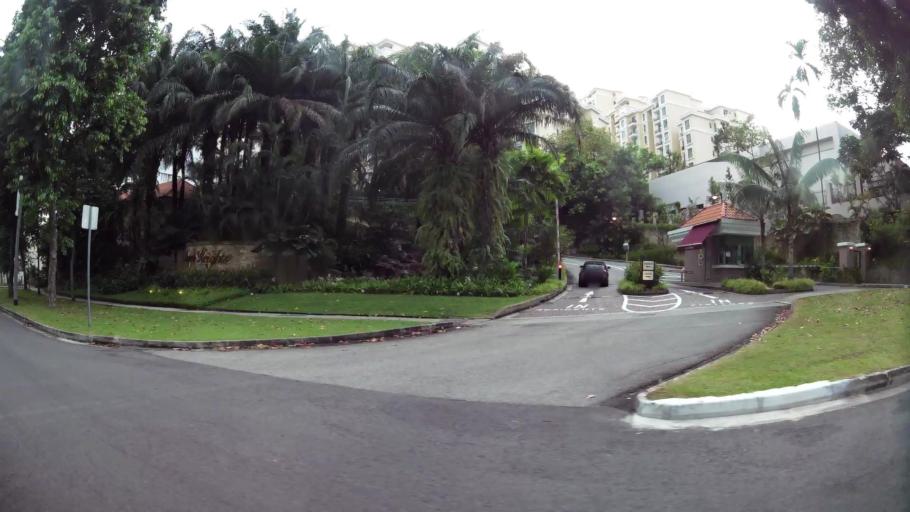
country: SG
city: Singapore
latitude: 1.2955
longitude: 103.8414
